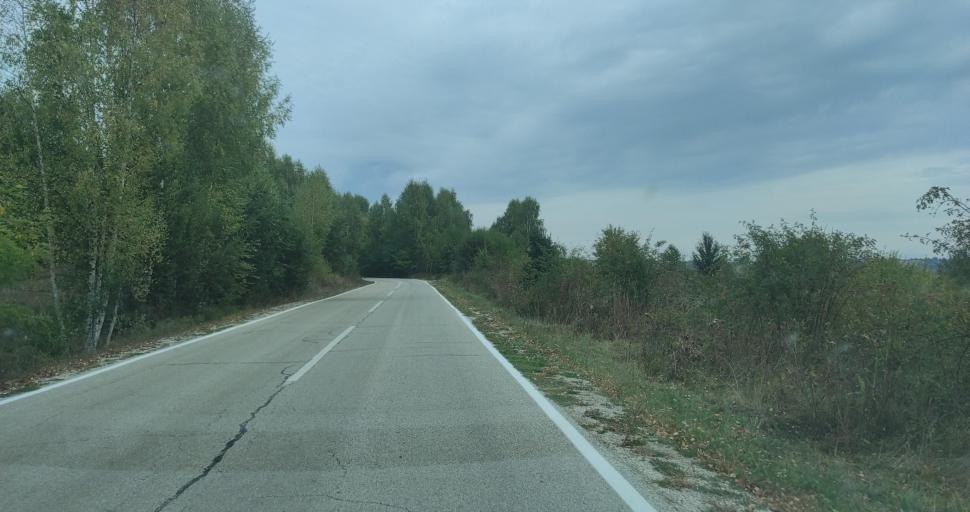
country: RS
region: Central Serbia
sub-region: Jablanicki Okrug
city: Crna Trava
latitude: 42.7196
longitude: 22.3334
